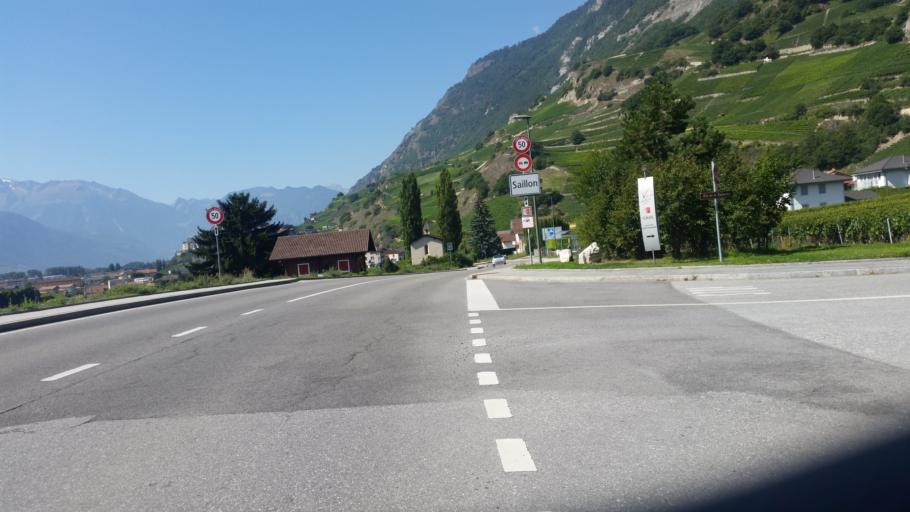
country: CH
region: Valais
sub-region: Martigny District
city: Saillon
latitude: 46.1778
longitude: 7.1957
